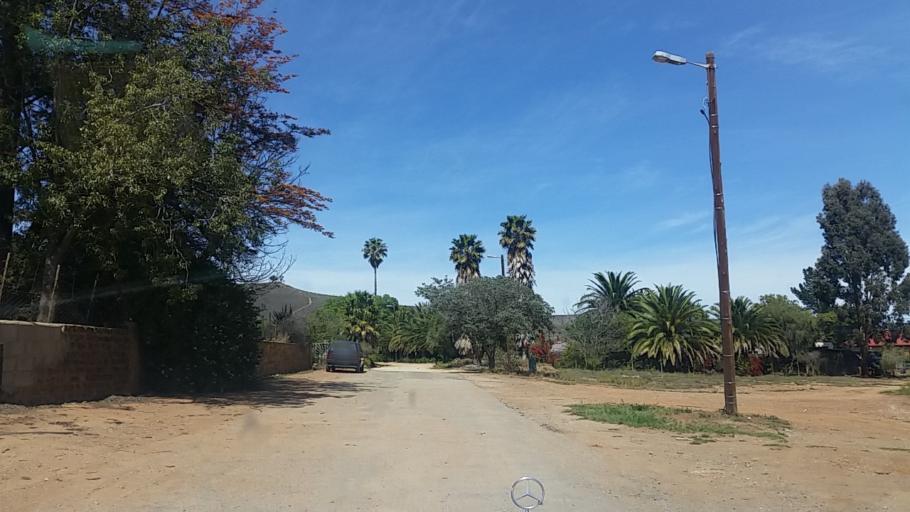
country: ZA
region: Western Cape
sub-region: Eden District Municipality
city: Knysna
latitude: -33.6492
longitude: 23.1358
